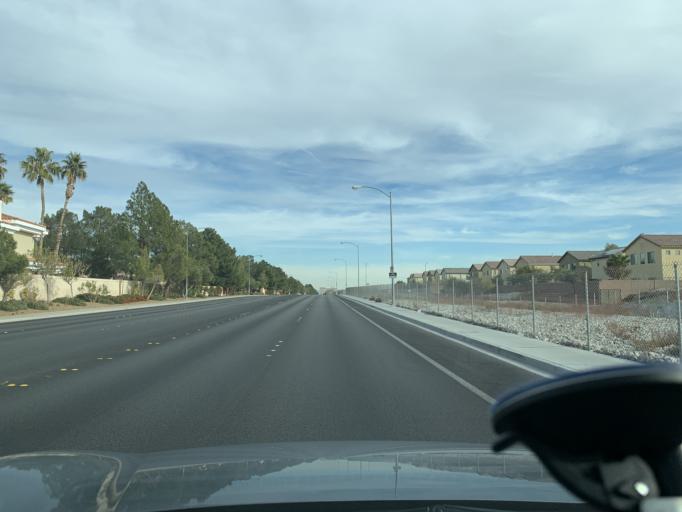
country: US
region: Nevada
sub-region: Clark County
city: Spring Valley
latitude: 36.0922
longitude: -115.2605
